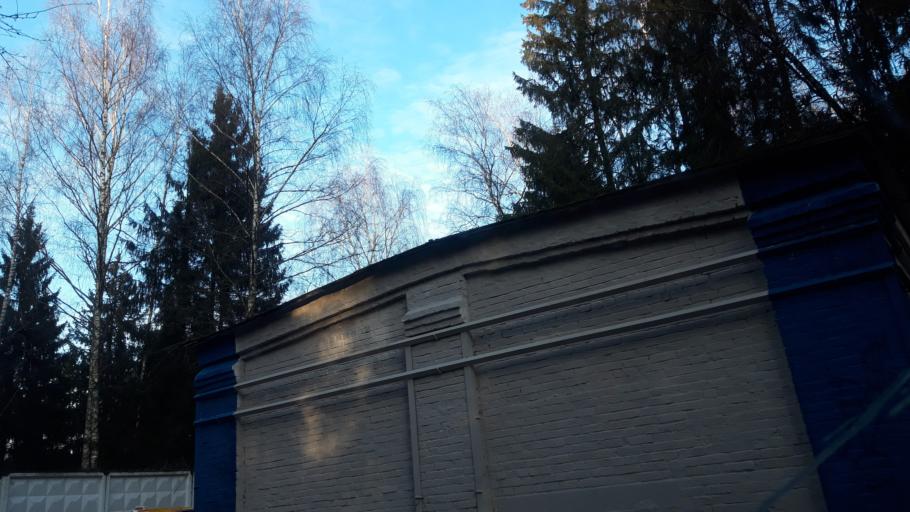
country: RU
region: Moskovskaya
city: Rzhavki
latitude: 56.0016
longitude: 37.2269
